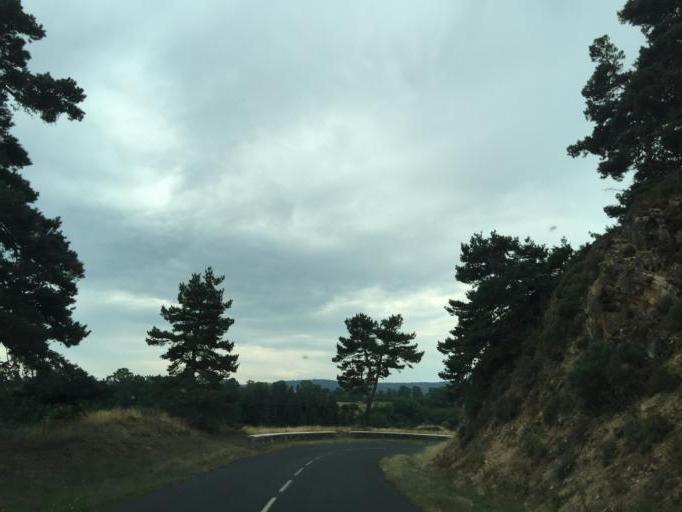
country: FR
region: Languedoc-Roussillon
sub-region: Departement de la Lozere
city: Langogne
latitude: 44.8195
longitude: 3.7774
